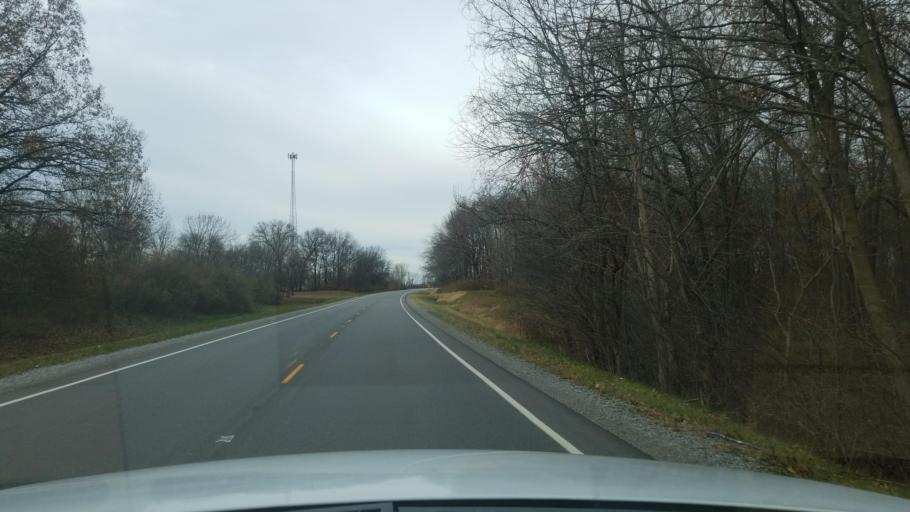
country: US
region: Illinois
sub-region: White County
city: Carmi
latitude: 37.9099
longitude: -88.1336
